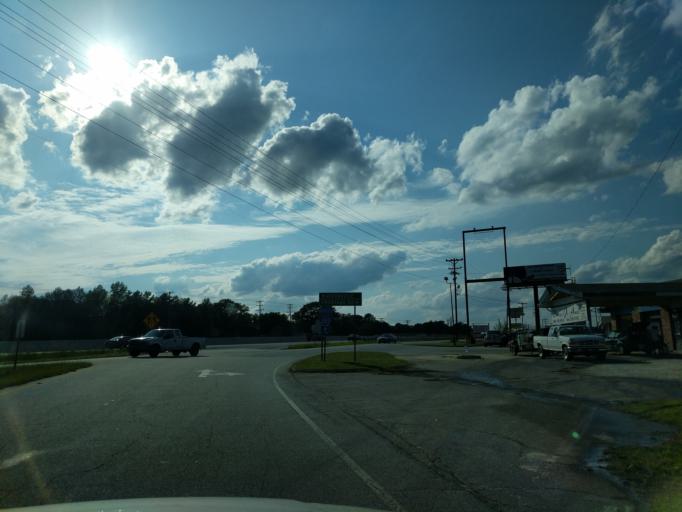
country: US
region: South Carolina
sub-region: Greenville County
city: Fountain Inn
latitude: 34.6897
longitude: -82.2191
